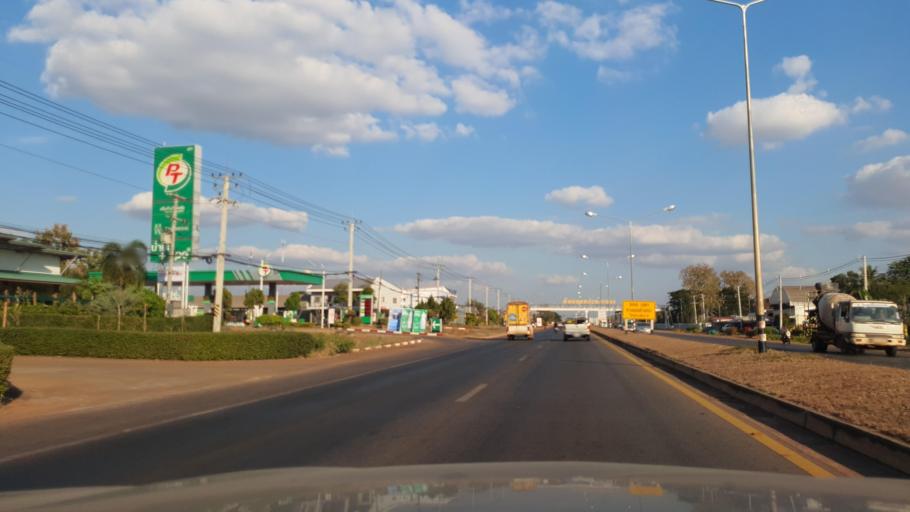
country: TH
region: Sakon Nakhon
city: Sakon Nakhon
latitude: 17.2568
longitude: 104.1698
